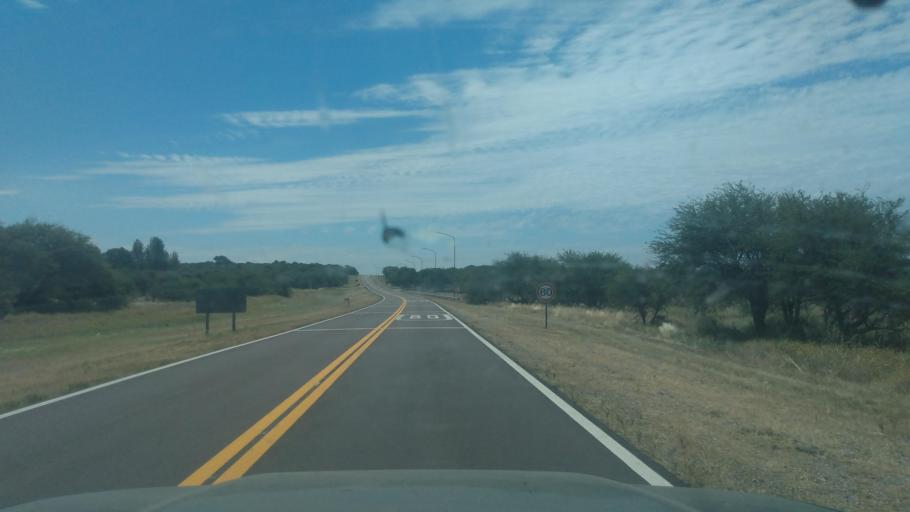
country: AR
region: La Pampa
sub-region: Departamento de Toay
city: Toay
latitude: -36.9182
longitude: -64.2836
